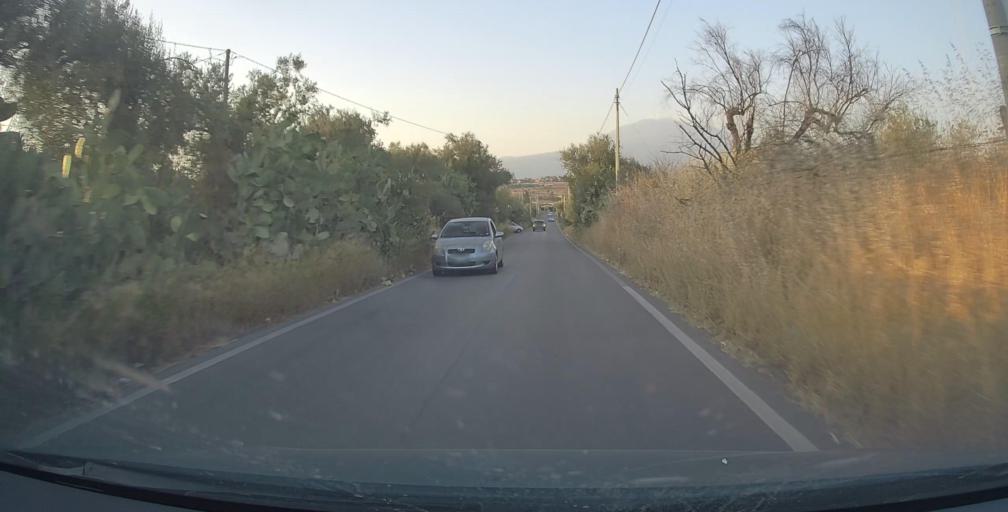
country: IT
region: Sicily
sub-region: Catania
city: Palazzolo
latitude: 37.5432
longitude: 14.9301
